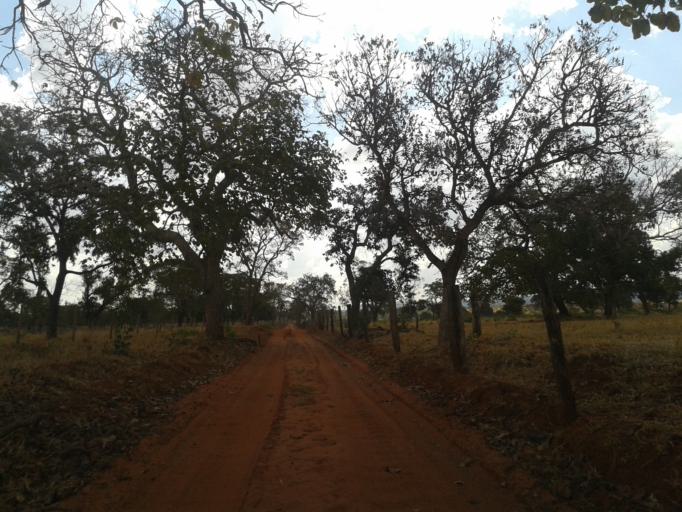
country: BR
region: Minas Gerais
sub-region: Santa Vitoria
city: Santa Vitoria
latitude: -19.1927
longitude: -49.9751
